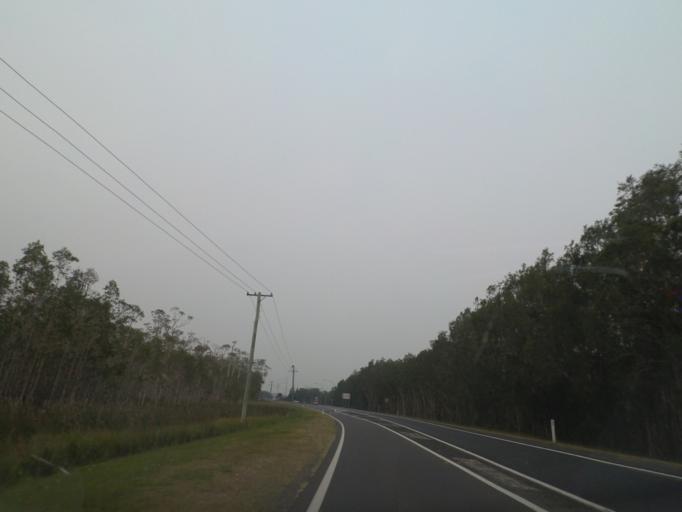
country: AU
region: New South Wales
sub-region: Coffs Harbour
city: Coffs Harbour
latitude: -30.3187
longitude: 153.1092
